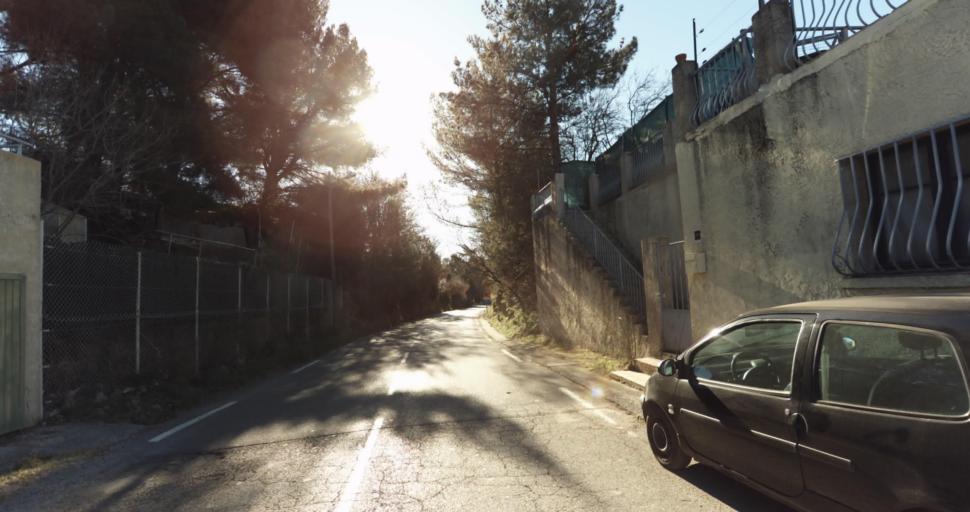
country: FR
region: Provence-Alpes-Cote d'Azur
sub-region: Departement des Bouches-du-Rhone
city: Cadolive
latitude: 43.3949
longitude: 5.5511
